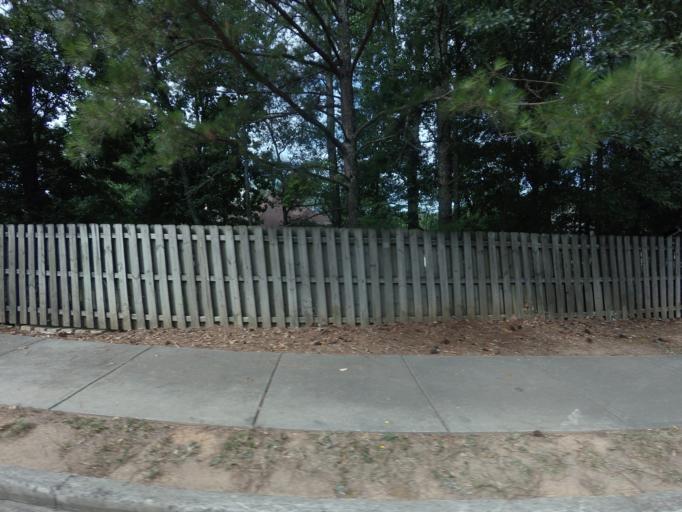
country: US
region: Georgia
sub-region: Gwinnett County
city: Duluth
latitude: 34.0412
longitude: -84.1576
